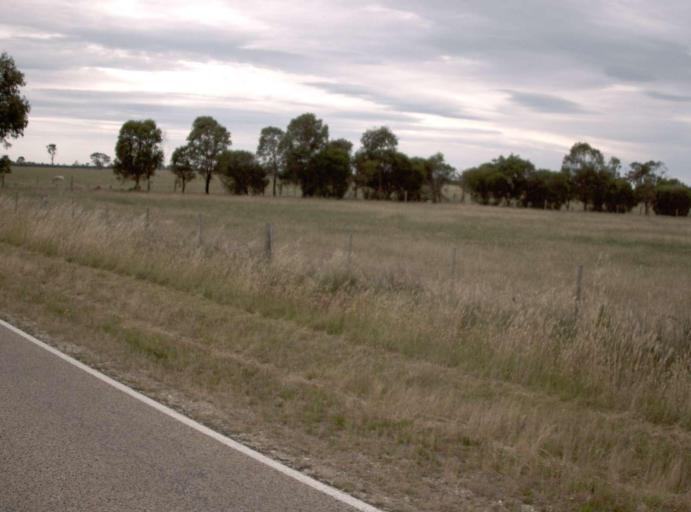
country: AU
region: Victoria
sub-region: East Gippsland
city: Bairnsdale
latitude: -37.9538
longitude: 147.5118
